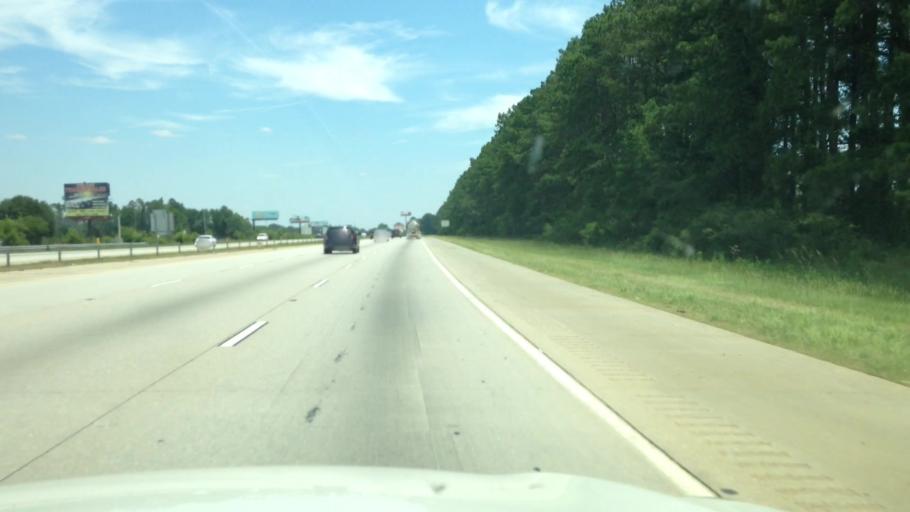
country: US
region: South Carolina
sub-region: Florence County
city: Florence
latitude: 34.2400
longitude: -79.7848
